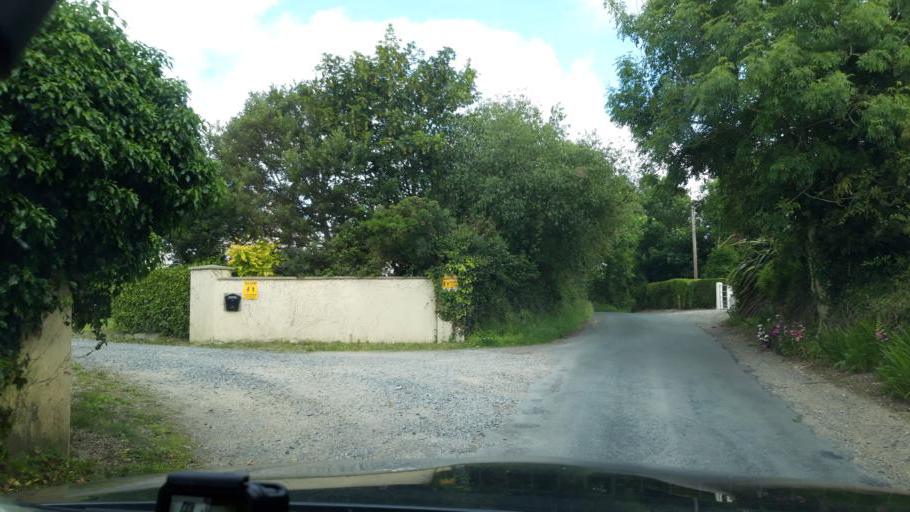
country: IE
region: Leinster
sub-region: Loch Garman
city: Loch Garman
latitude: 52.2829
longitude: -6.4979
